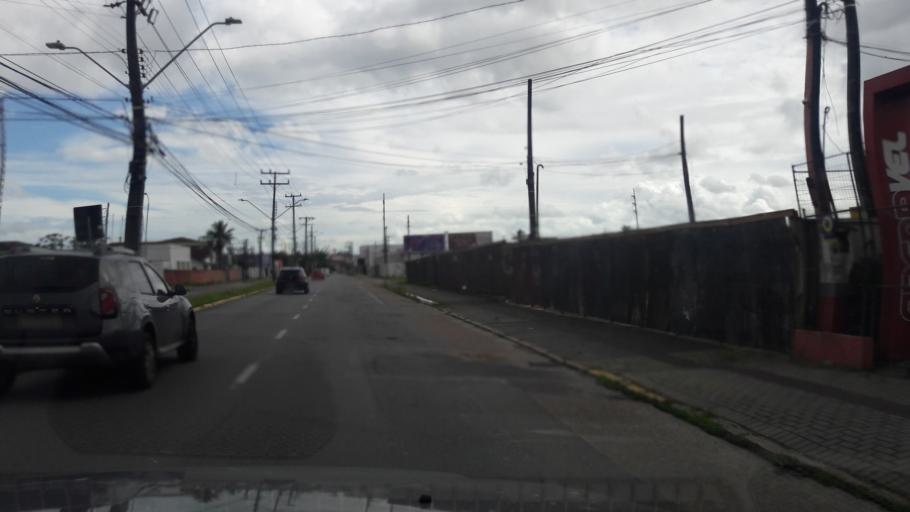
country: BR
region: Santa Catarina
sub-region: Joinville
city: Joinville
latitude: -26.3170
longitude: -48.8405
